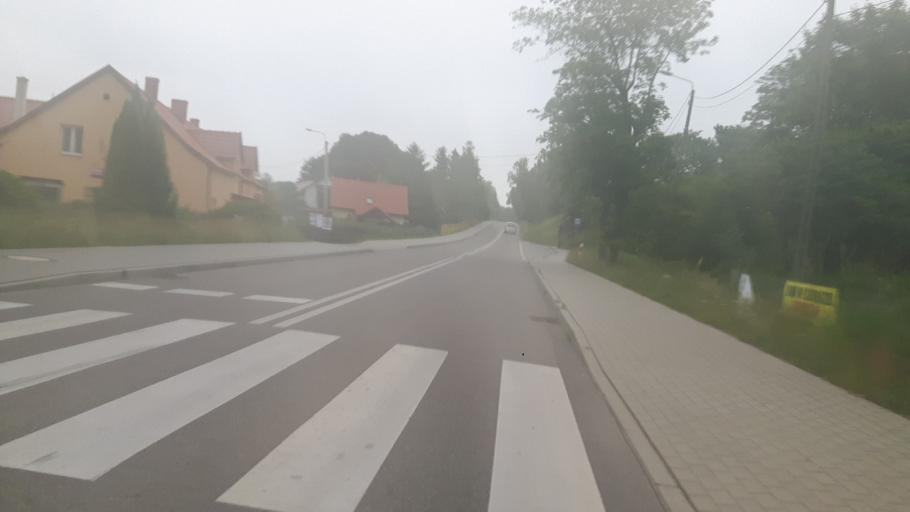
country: PL
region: Warmian-Masurian Voivodeship
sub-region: Powiat elblaski
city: Elblag
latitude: 54.2615
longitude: 19.4046
